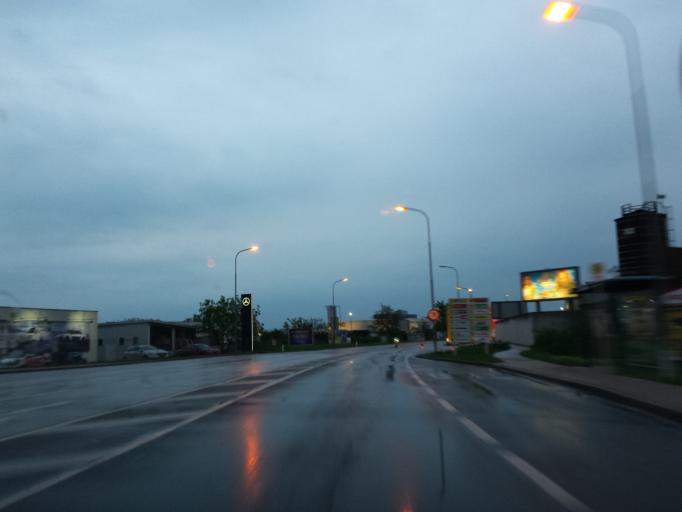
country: AT
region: Lower Austria
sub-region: Politischer Bezirk Modling
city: Brunn am Gebirge
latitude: 48.1121
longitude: 16.3046
